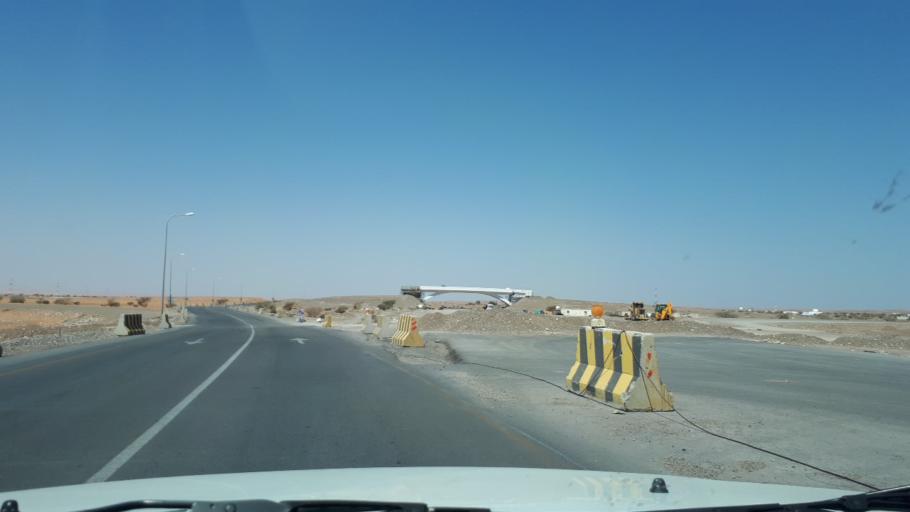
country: OM
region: Ash Sharqiyah
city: Badiyah
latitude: 22.4957
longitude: 58.9510
